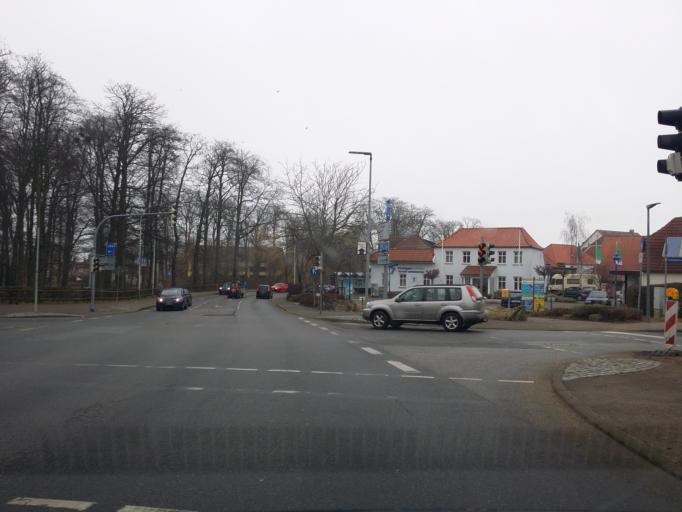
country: DE
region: Schleswig-Holstein
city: Heiligenhafen
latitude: 54.3711
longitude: 10.9728
